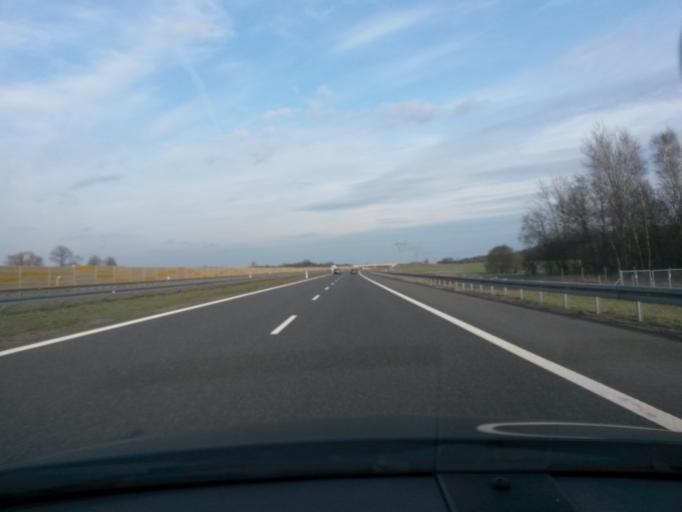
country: PL
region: Lodz Voivodeship
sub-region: Powiat zgierski
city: Ozorkow
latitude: 51.9282
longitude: 19.3089
